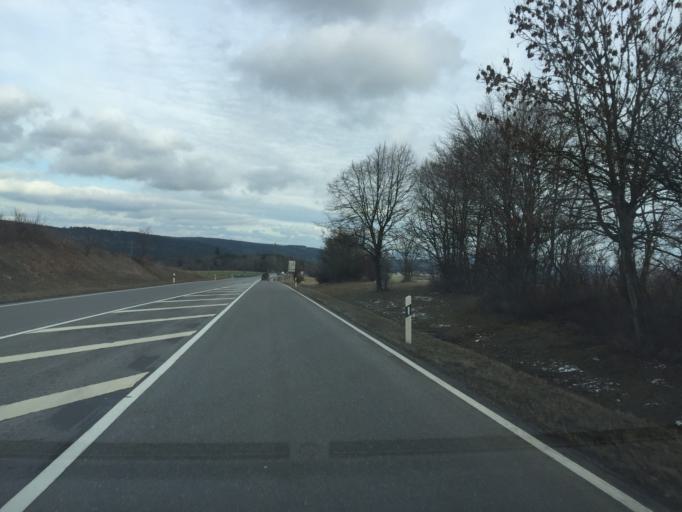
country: DE
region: Baden-Wuerttemberg
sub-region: Freiburg Region
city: Loffingen
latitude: 47.8868
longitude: 8.3661
